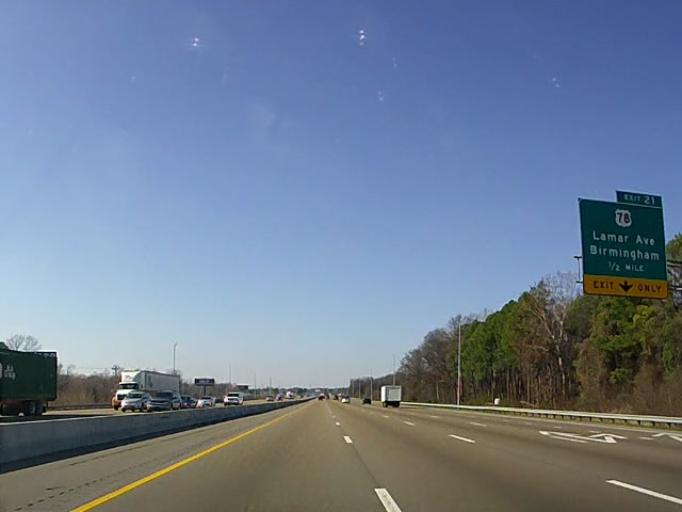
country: US
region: Tennessee
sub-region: Shelby County
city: New South Memphis
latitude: 35.0815
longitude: -89.9407
